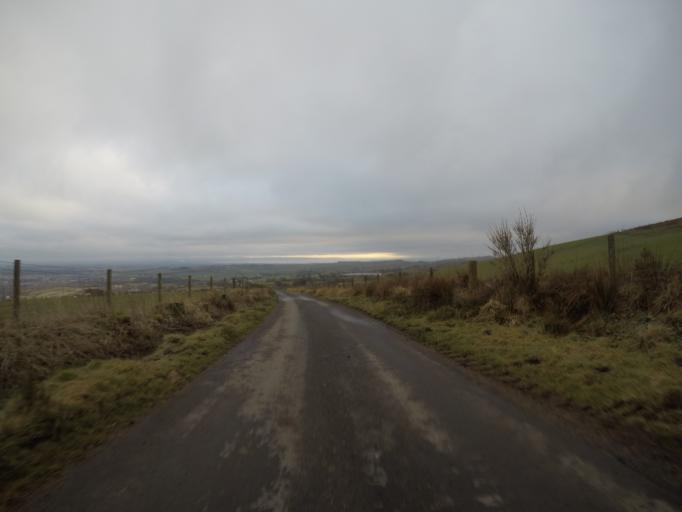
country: GB
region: Scotland
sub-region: North Ayrshire
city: Dalry
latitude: 55.7293
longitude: -4.7641
